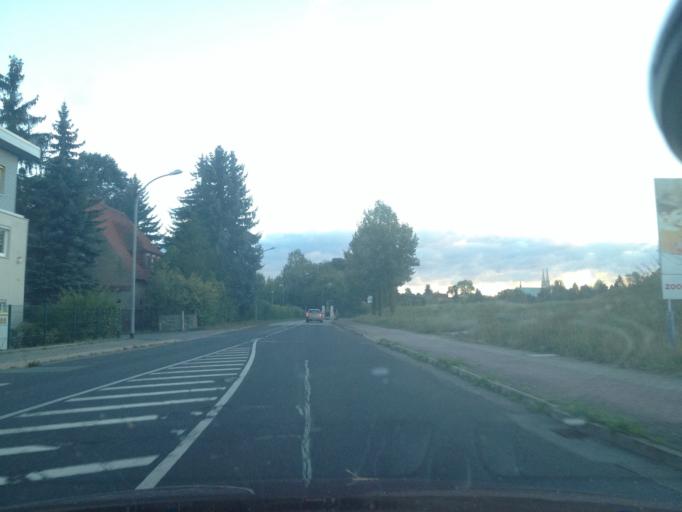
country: DE
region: Saxony
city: Goerlitz
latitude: 51.1693
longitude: 14.9983
